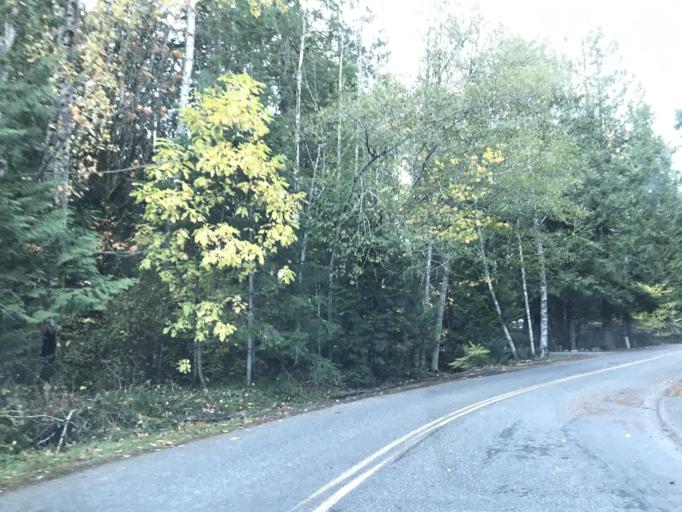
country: US
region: Washington
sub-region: Whatcom County
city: Geneva
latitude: 48.7423
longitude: -122.4152
